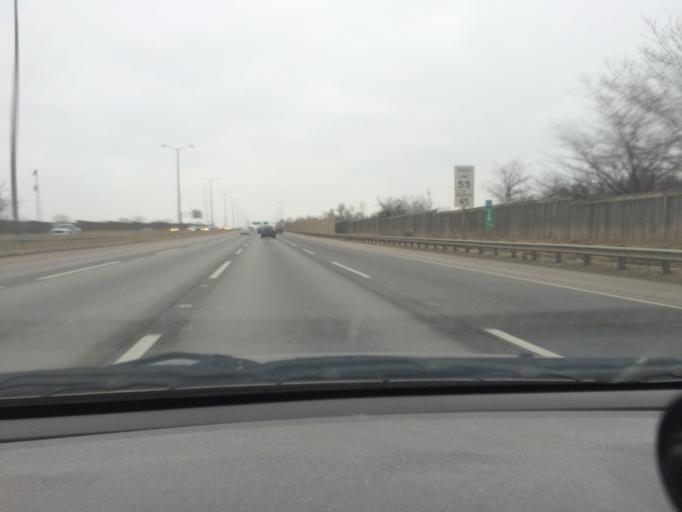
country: US
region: Illinois
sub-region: DuPage County
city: Glendale Heights
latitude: 41.9124
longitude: -88.0378
